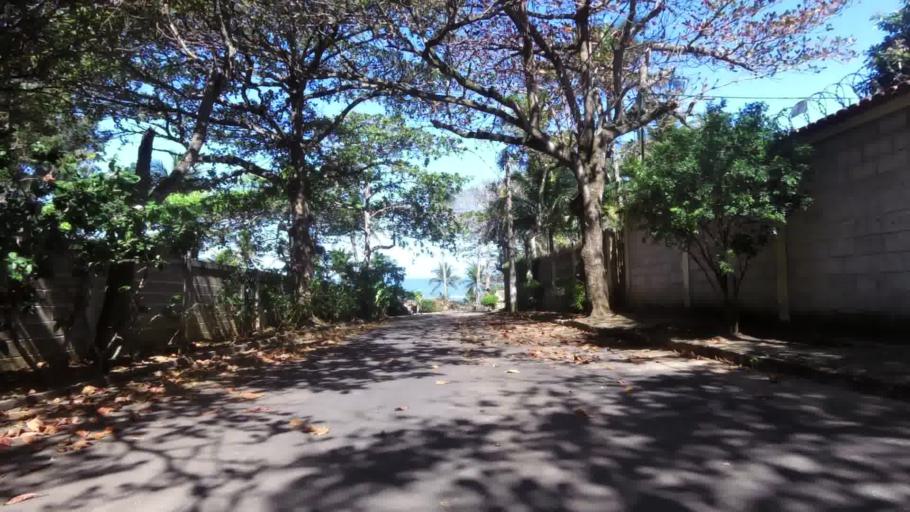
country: BR
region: Espirito Santo
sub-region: Guarapari
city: Guarapari
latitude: -20.7380
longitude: -40.5345
